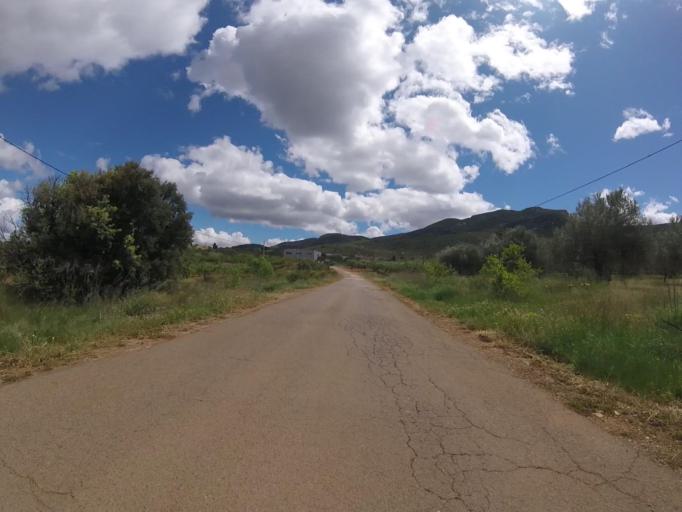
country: ES
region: Valencia
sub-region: Provincia de Castello
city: Sierra-Engarceran
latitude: 40.2908
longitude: -0.0520
